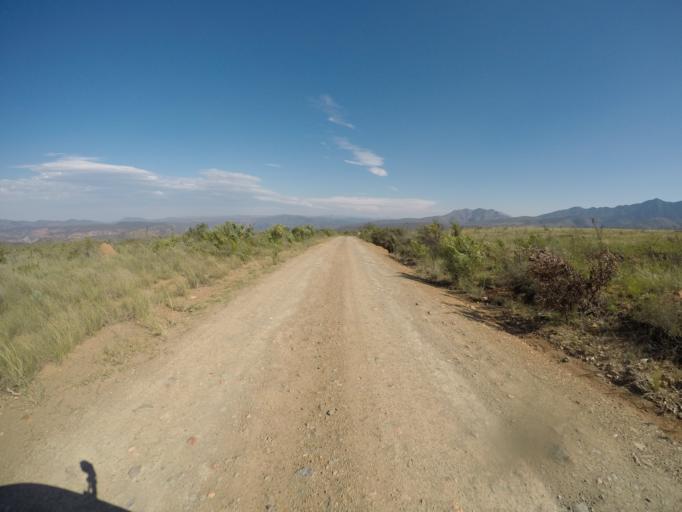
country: ZA
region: Eastern Cape
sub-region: Cacadu District Municipality
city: Kareedouw
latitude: -33.6347
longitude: 24.4739
